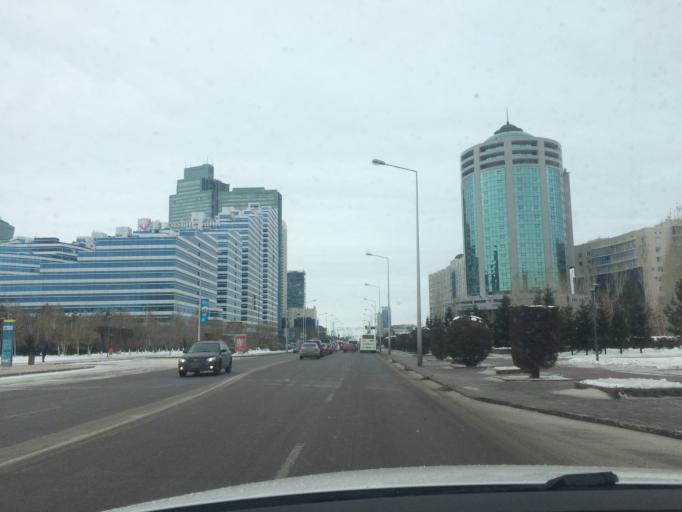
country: KZ
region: Astana Qalasy
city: Astana
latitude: 51.1306
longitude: 71.4319
